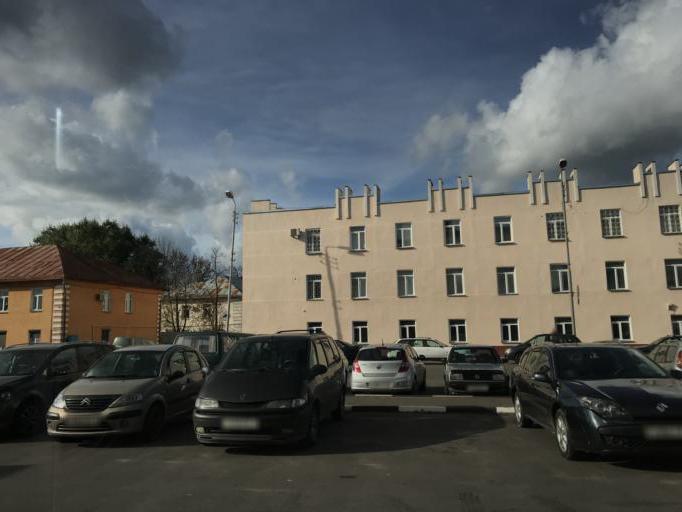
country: BY
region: Gomel
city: Gomel
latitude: 52.4507
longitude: 30.9766
